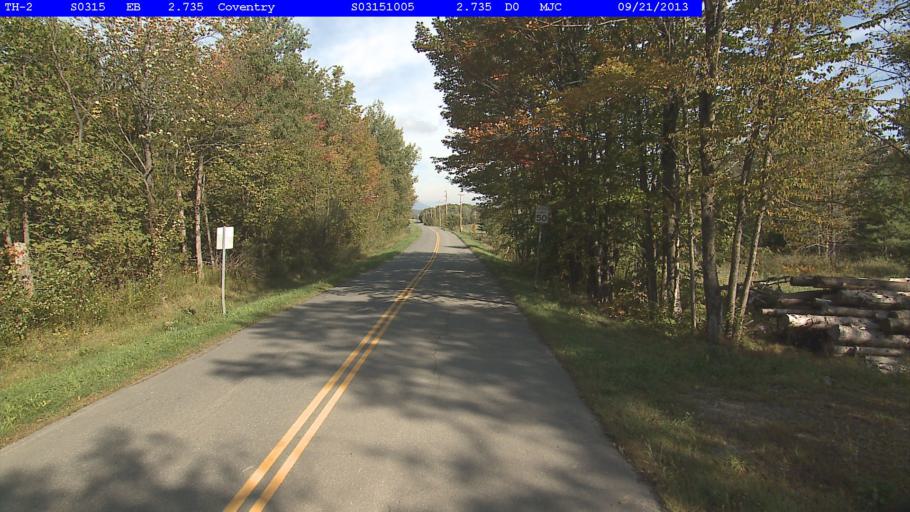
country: US
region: Vermont
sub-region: Orleans County
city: Newport
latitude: 44.8757
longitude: -72.2154
